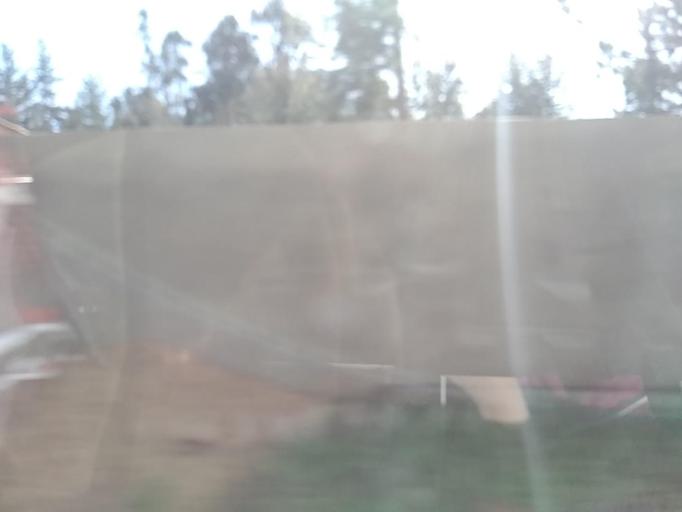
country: CL
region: Valparaiso
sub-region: San Antonio Province
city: El Tabo
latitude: -33.4154
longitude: -71.6191
